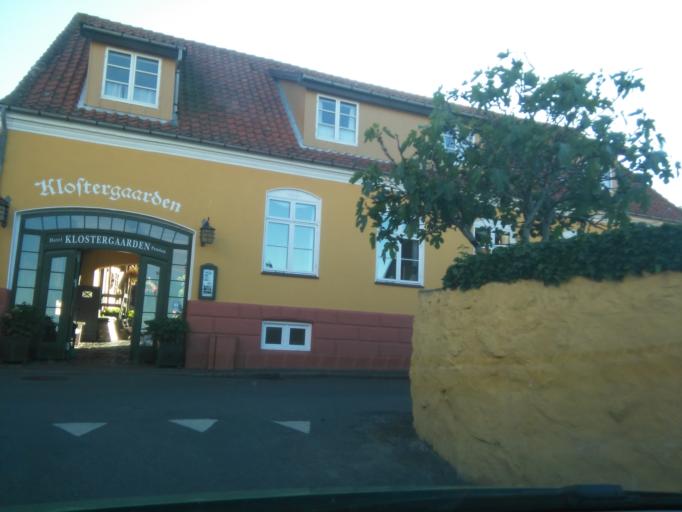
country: DK
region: Capital Region
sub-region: Bornholm Kommune
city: Ronne
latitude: 55.2761
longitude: 14.8043
